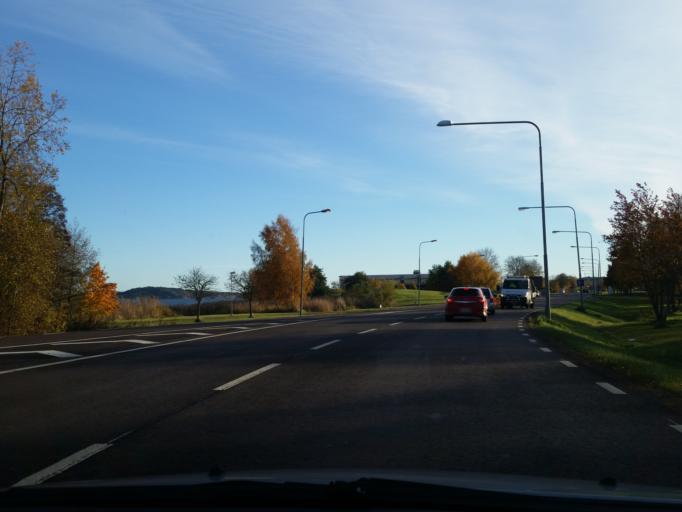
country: AX
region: Mariehamns stad
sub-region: Mariehamn
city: Mariehamn
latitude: 60.1120
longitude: 19.9427
